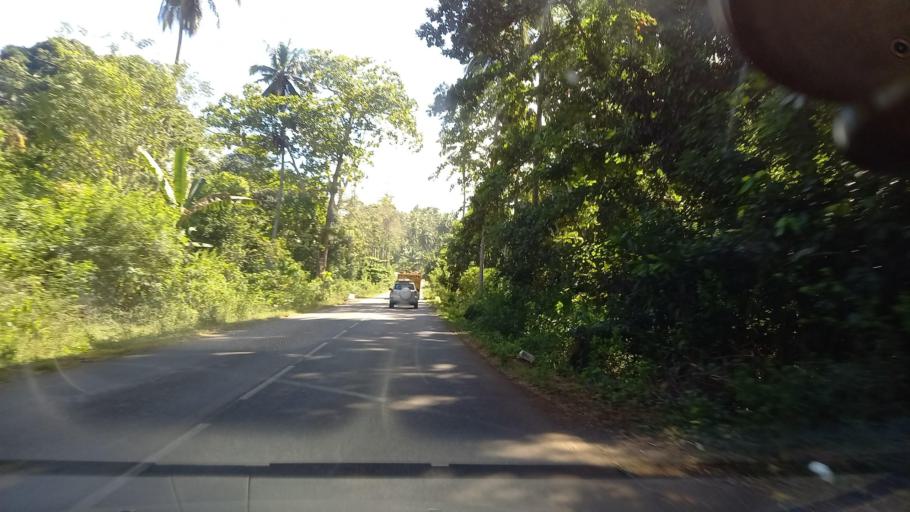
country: YT
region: M'Tsangamouji
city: M'Tsangamouji
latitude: -12.7569
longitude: 45.0958
